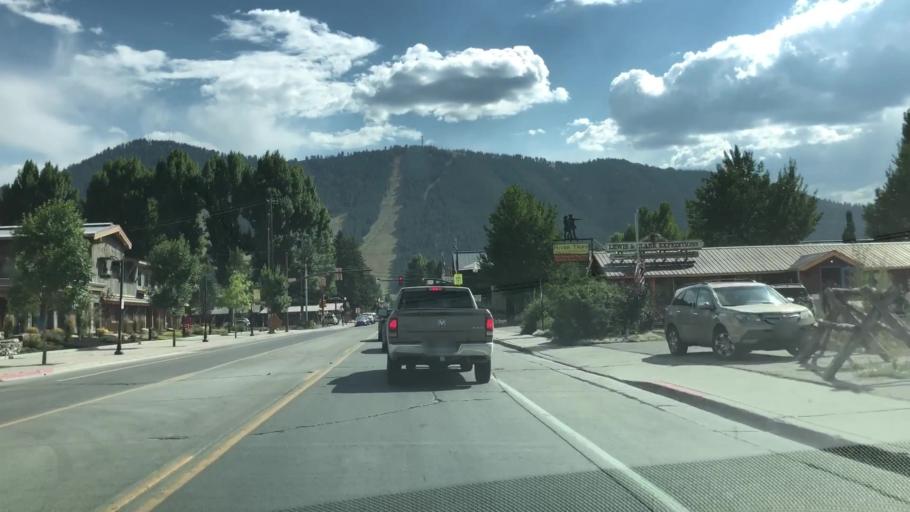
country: US
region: Wyoming
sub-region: Teton County
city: Jackson
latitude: 43.4844
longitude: -110.7624
